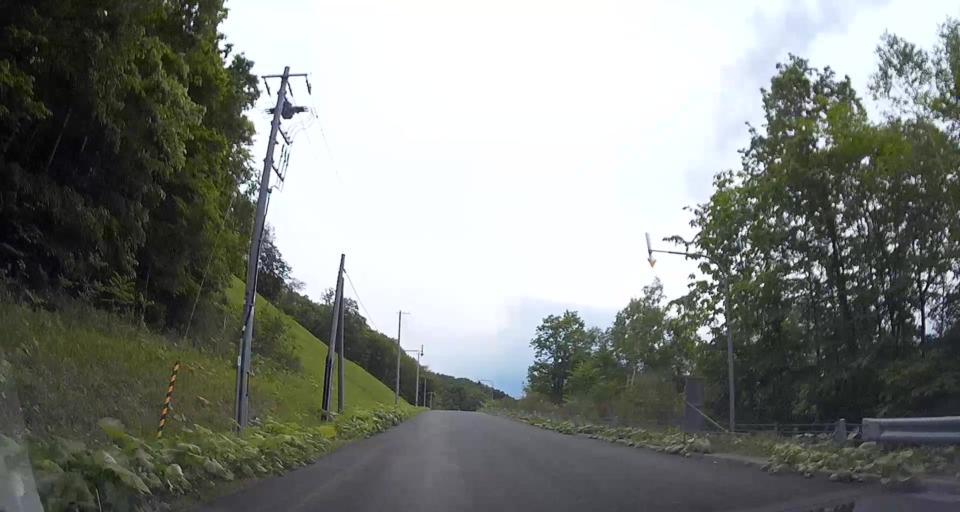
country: JP
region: Hokkaido
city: Chitose
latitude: 42.7739
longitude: 142.0075
